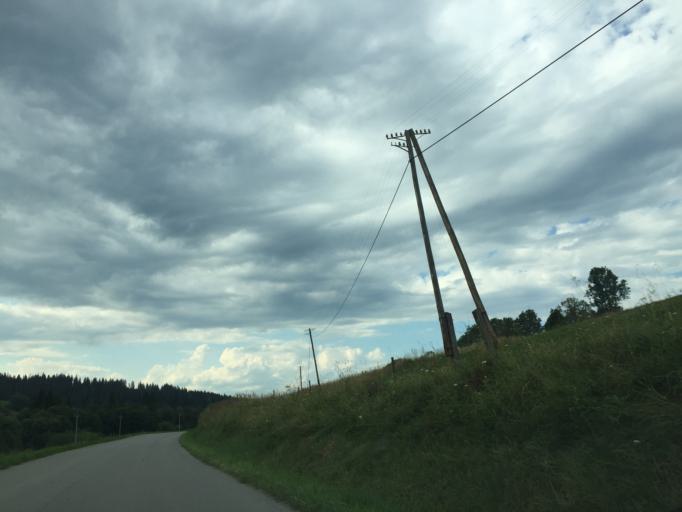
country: PL
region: Silesian Voivodeship
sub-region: Powiat zywiecki
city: Korbielow
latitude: 49.4308
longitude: 19.3203
